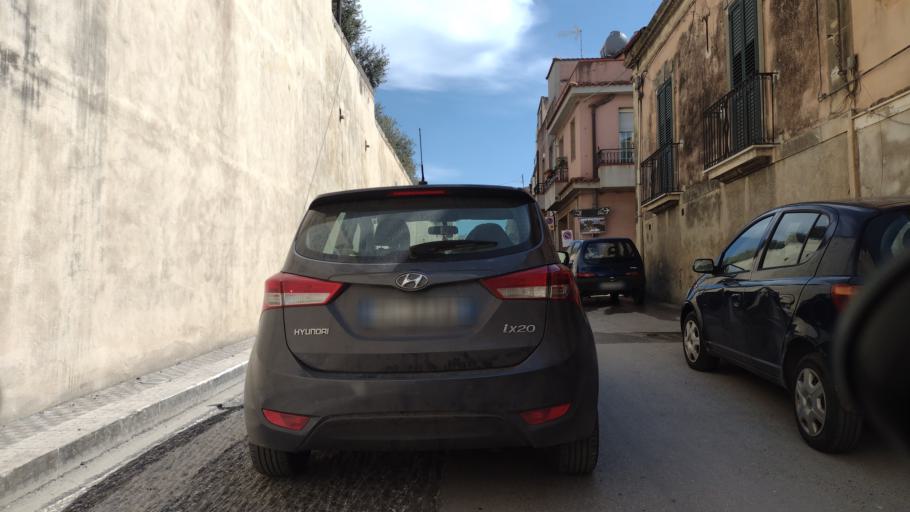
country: IT
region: Sicily
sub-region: Provincia di Siracusa
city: Noto
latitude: 36.8903
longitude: 15.0637
